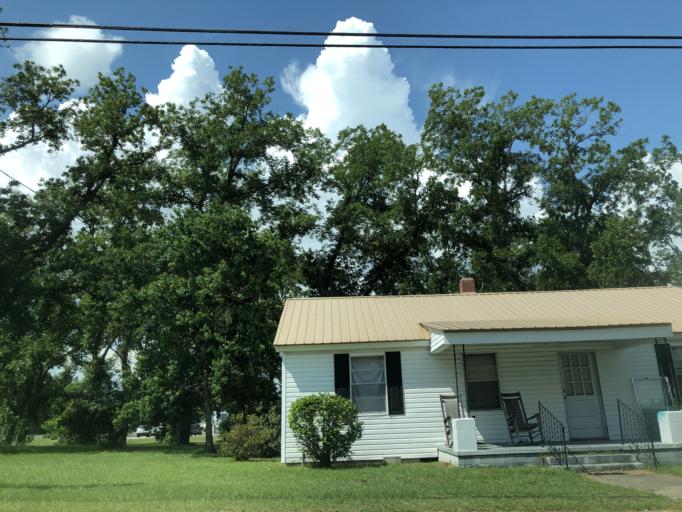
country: US
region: Georgia
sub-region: Telfair County
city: McRae
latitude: 32.0656
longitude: -82.8930
